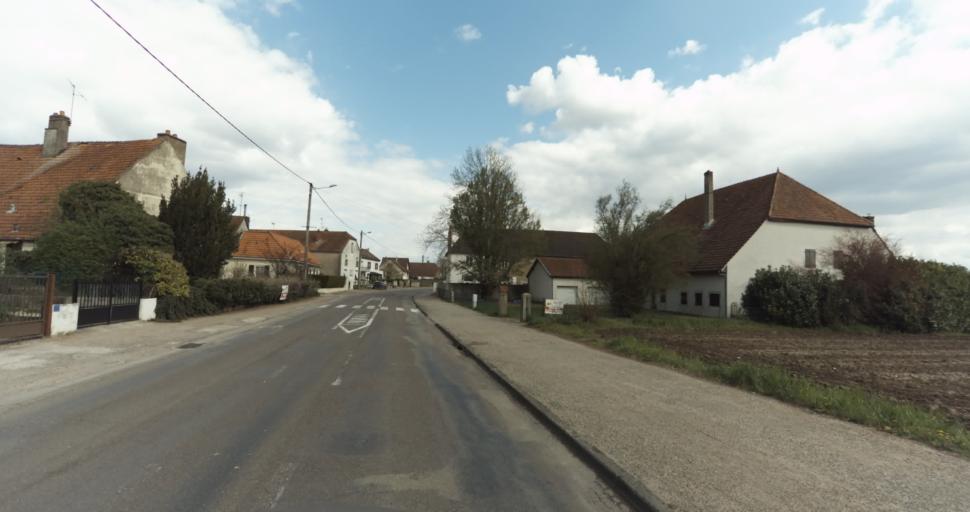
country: FR
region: Bourgogne
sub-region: Departement de la Cote-d'Or
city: Auxonne
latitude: 47.1936
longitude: 5.3992
